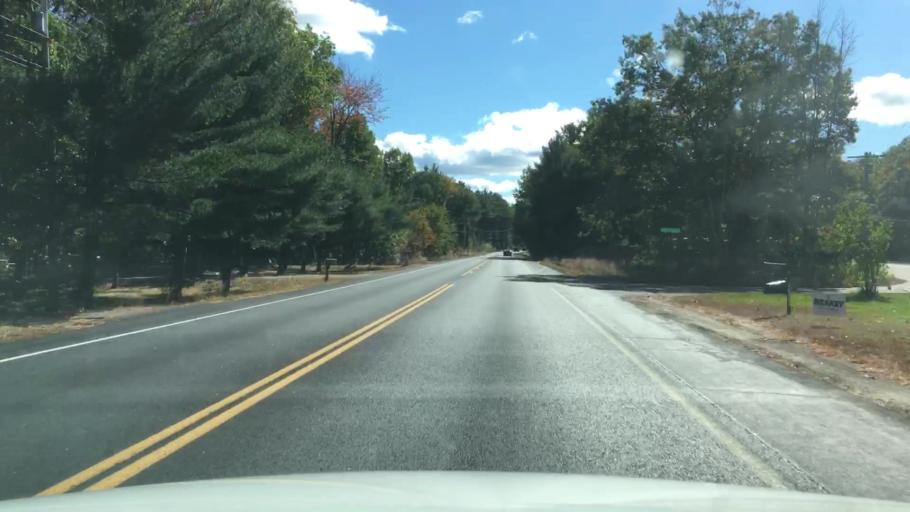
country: US
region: Maine
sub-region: York County
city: South Sanford
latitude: 43.4313
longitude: -70.7334
